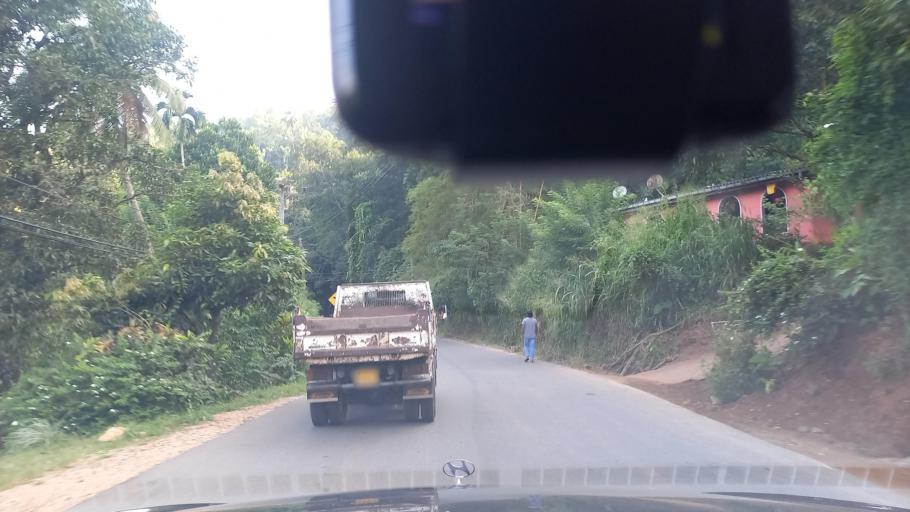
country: LK
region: Central
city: Kandy
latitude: 7.2342
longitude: 80.6025
